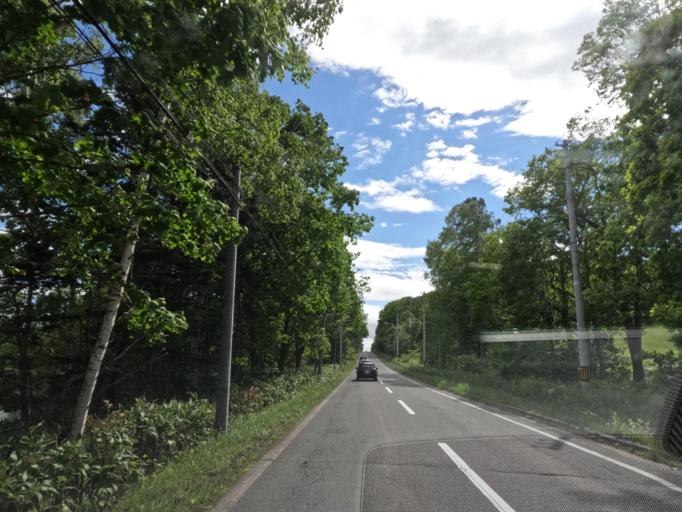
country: JP
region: Hokkaido
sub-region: Asahikawa-shi
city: Asahikawa
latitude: 43.8360
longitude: 142.5382
